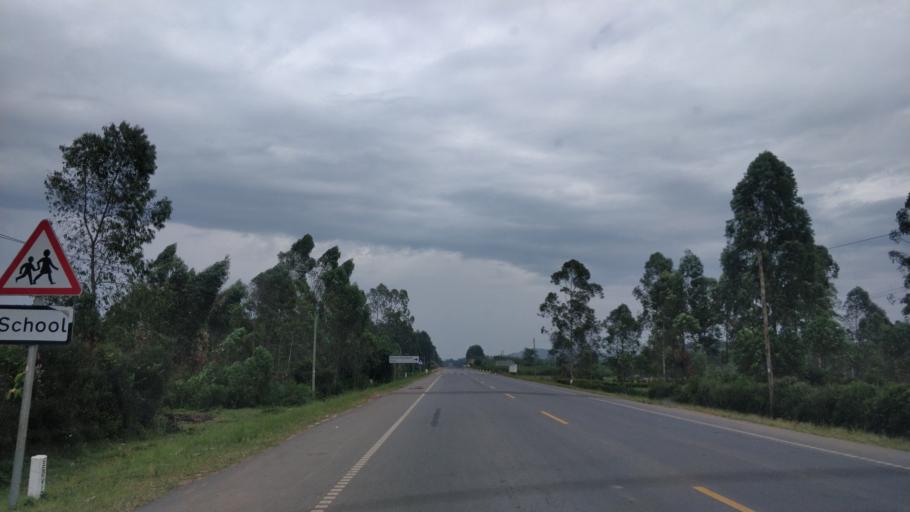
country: UG
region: Western Region
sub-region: Sheema District
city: Kibingo
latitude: -0.6719
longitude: 30.4309
